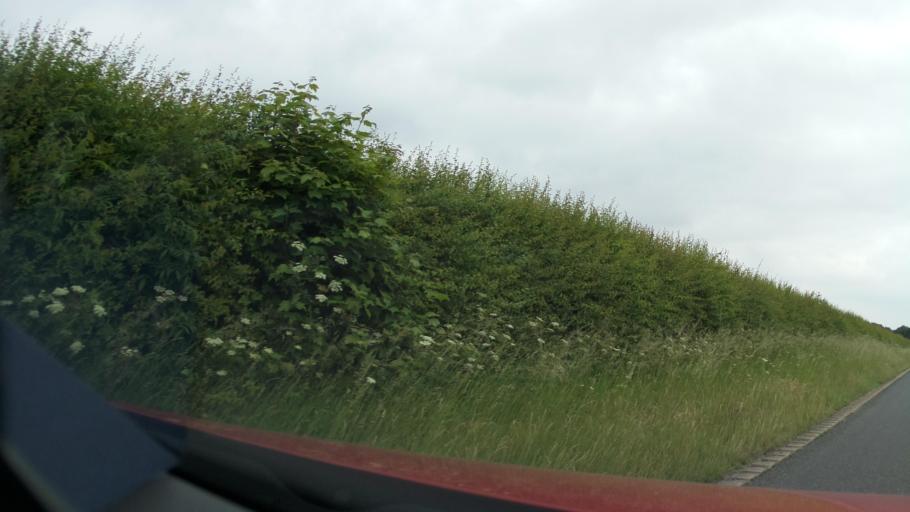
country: GB
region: England
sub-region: District of Rutland
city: Empingham
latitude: 52.6497
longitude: -0.6098
